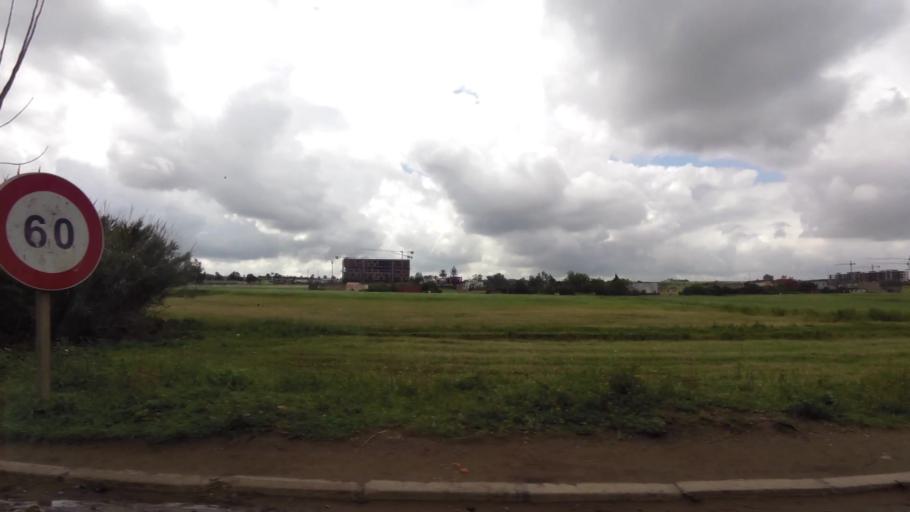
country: MA
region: Grand Casablanca
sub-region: Nouaceur
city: Bouskoura
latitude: 33.5154
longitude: -7.6347
